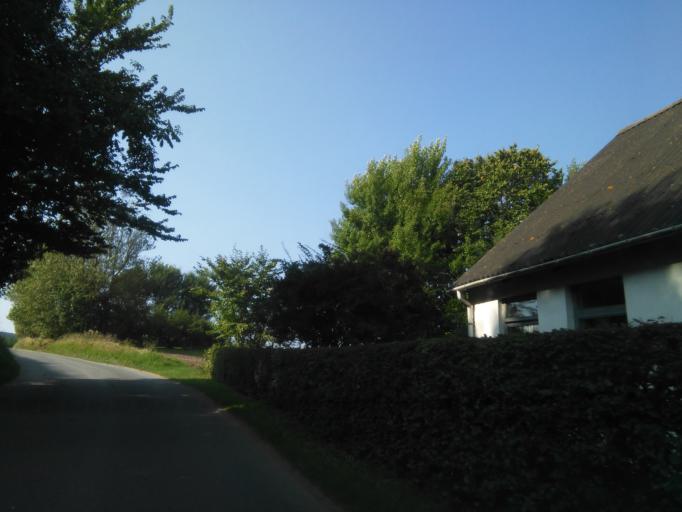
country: DK
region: Central Jutland
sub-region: Syddjurs Kommune
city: Ronde
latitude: 56.1888
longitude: 10.4198
